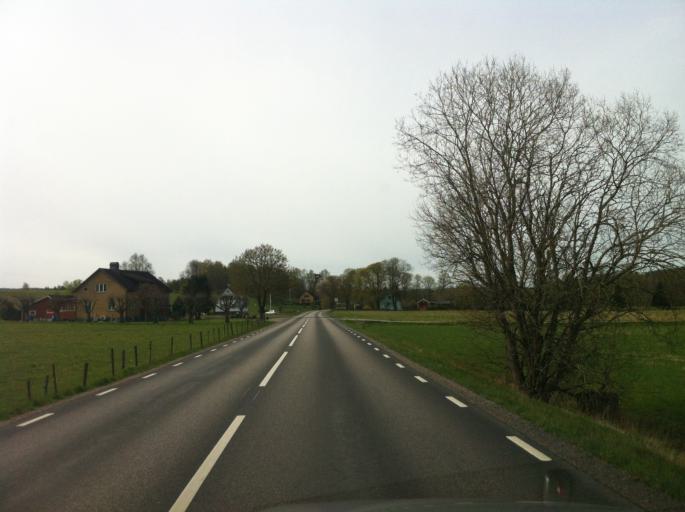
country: SE
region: Vaestra Goetaland
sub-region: Bollebygds Kommun
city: Bollebygd
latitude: 57.6877
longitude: 12.5679
